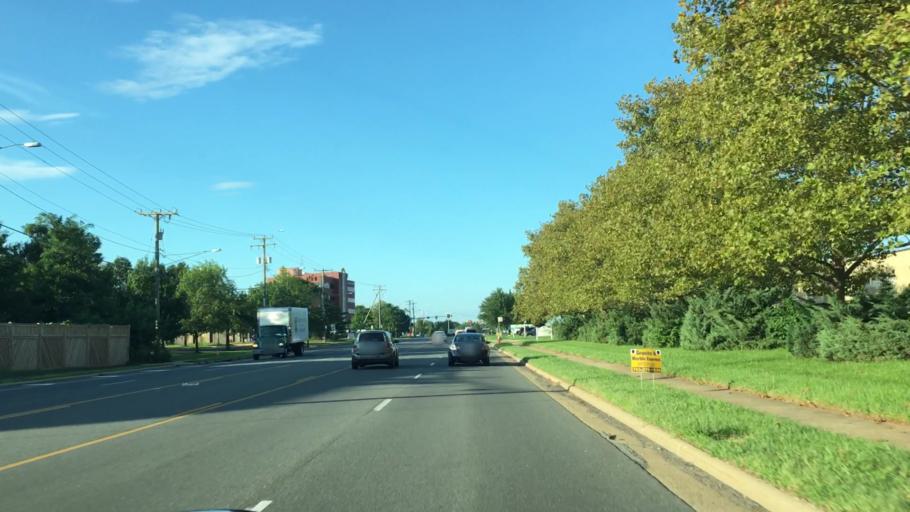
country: US
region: Virginia
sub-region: Fairfax County
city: Chantilly
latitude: 38.8896
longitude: -77.4334
